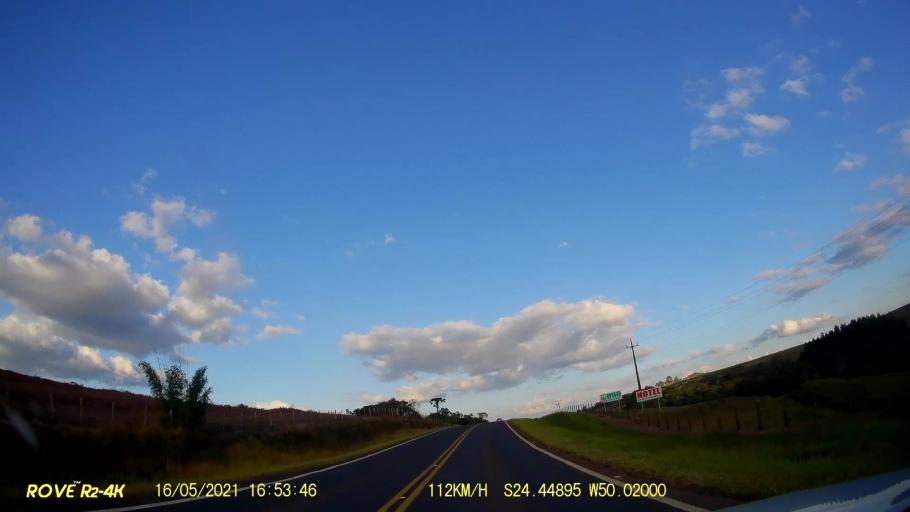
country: BR
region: Parana
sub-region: Pirai Do Sul
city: Pirai do Sul
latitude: -24.4492
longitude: -50.0194
